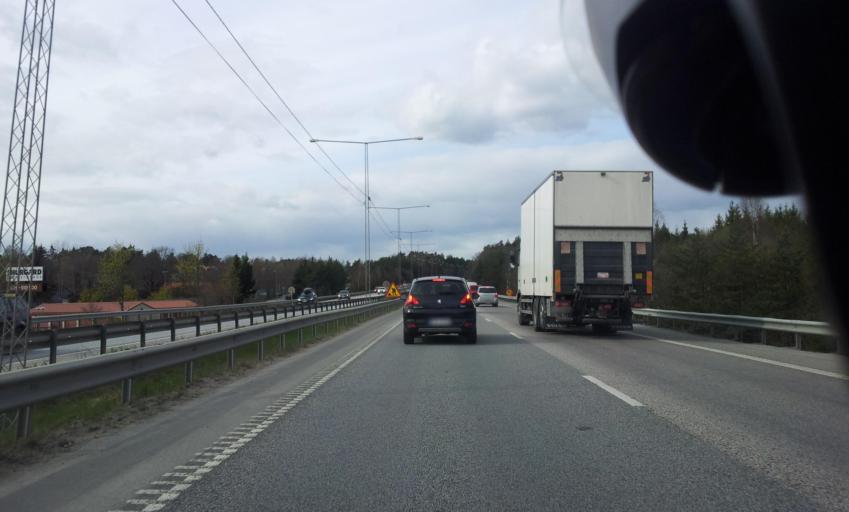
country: SE
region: Stockholm
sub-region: Jarfalla Kommun
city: Jakobsberg
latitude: 59.4304
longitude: 17.8480
